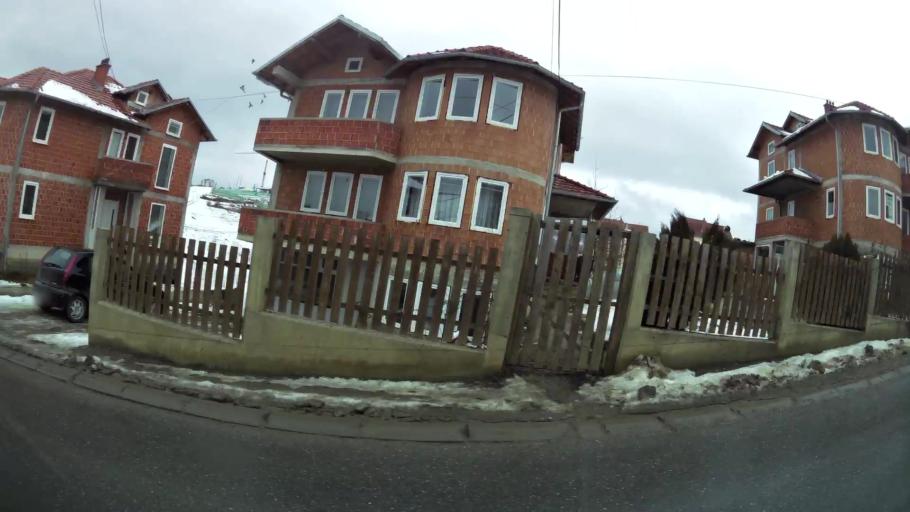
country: XK
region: Pristina
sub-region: Komuna e Prishtines
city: Pristina
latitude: 42.6460
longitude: 21.1864
